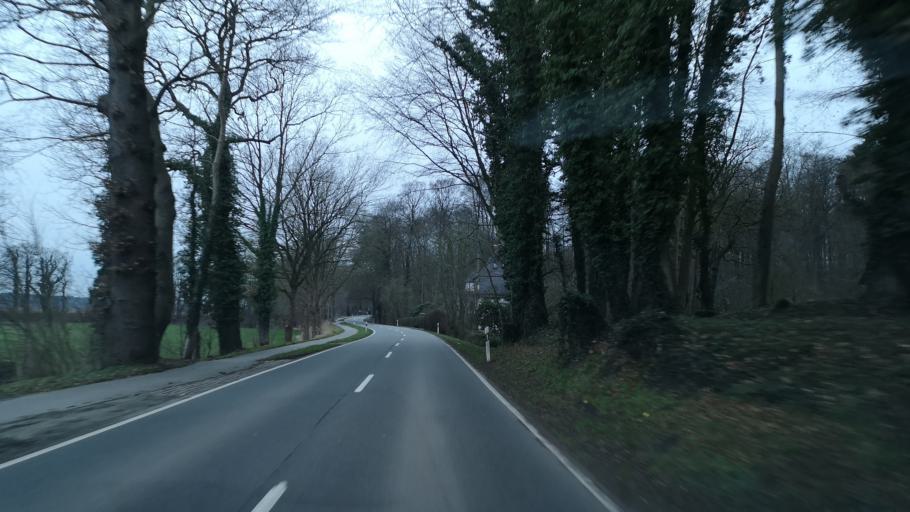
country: DE
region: Schleswig-Holstein
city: Munsterdorf
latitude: 53.9135
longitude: 9.5536
